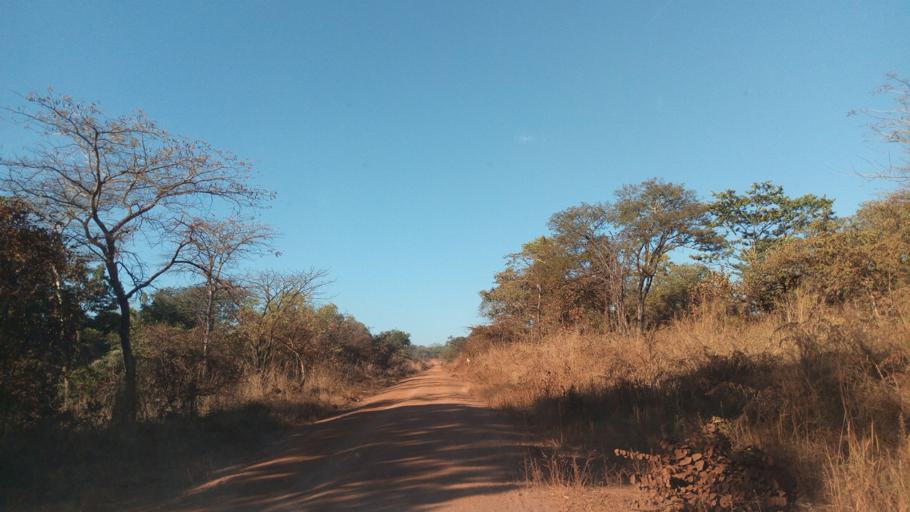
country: ZM
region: Luapula
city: Mwense
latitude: -10.5727
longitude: 28.4345
